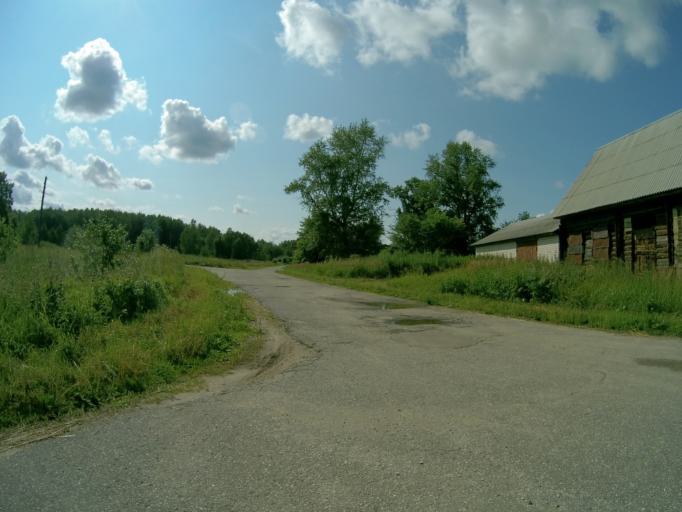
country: RU
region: Vladimir
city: Orgtrud
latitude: 56.2751
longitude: 40.6991
